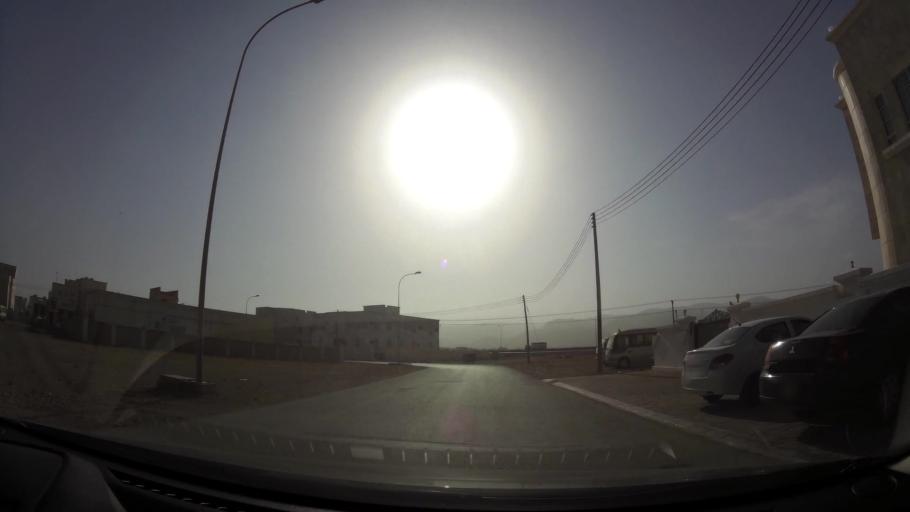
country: OM
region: Zufar
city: Salalah
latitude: 17.0244
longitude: 54.0217
